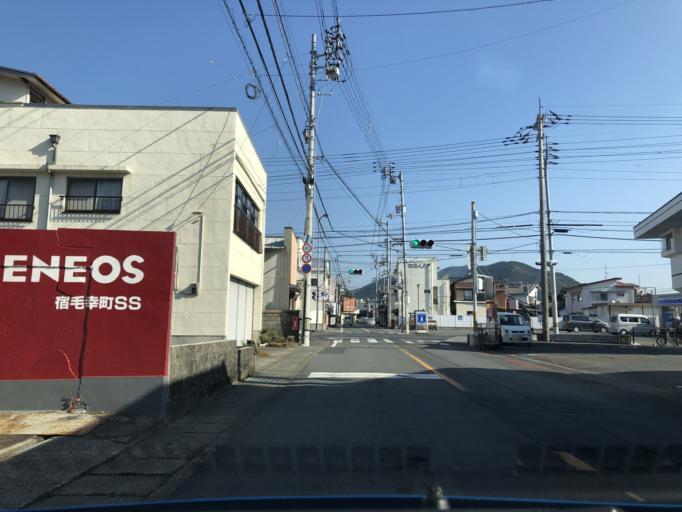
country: JP
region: Kochi
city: Sukumo
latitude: 32.9362
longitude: 132.7236
